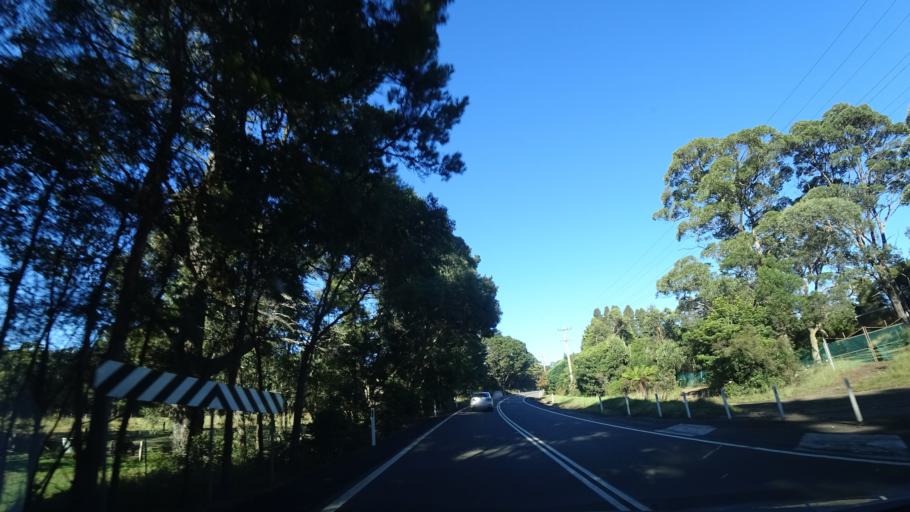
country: AU
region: New South Wales
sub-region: Blue Mountains Municipality
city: Lawson
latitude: -33.5367
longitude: 150.4430
